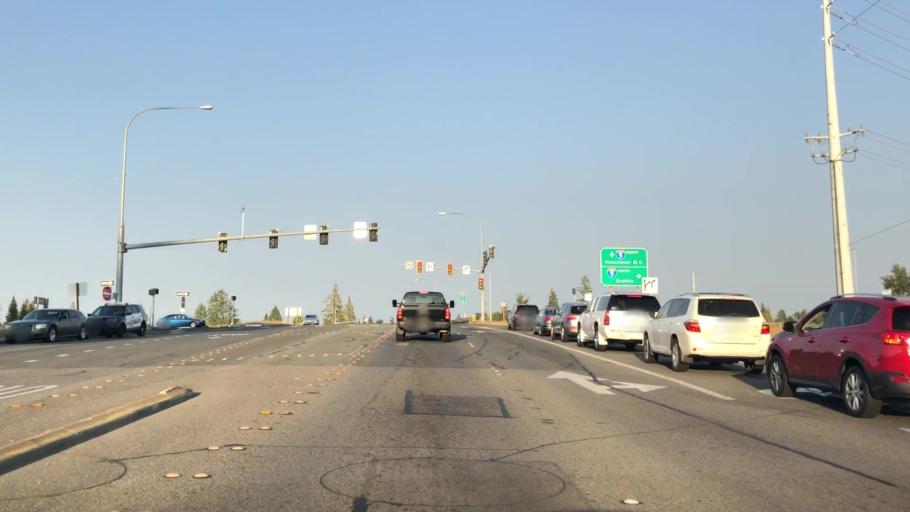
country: US
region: Washington
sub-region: Snohomish County
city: Marysville
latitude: 48.0758
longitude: -122.1874
